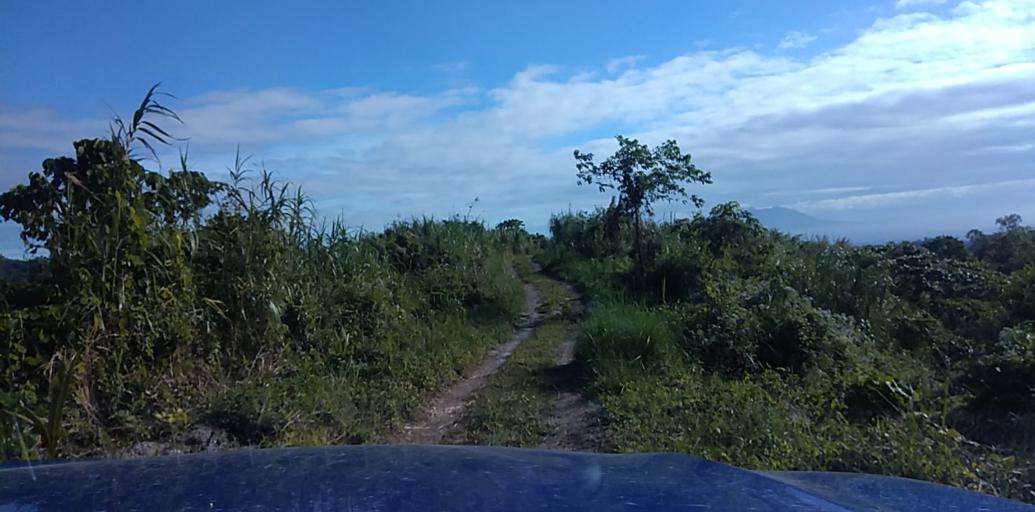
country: PH
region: Central Luzon
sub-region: Province of Pampanga
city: Babo-Pangulo
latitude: 15.1492
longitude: 120.4285
